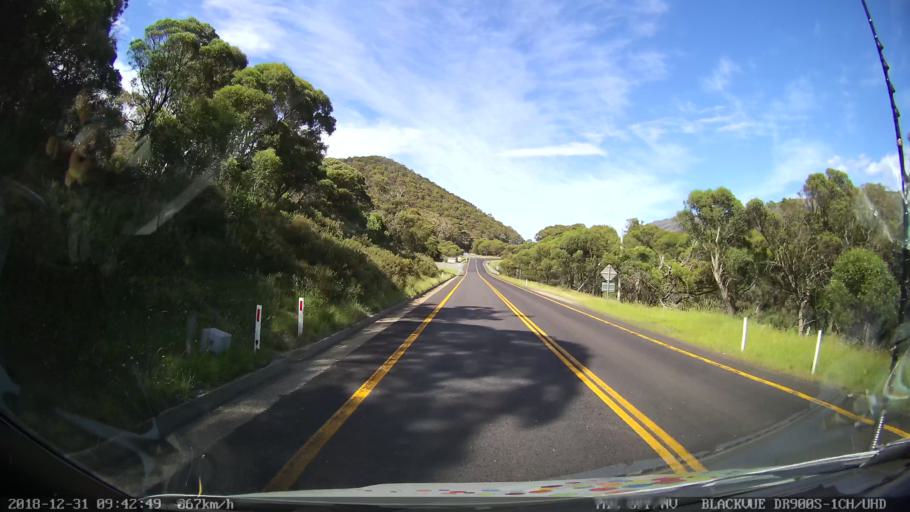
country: AU
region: New South Wales
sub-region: Snowy River
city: Jindabyne
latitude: -36.4987
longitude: 148.3188
